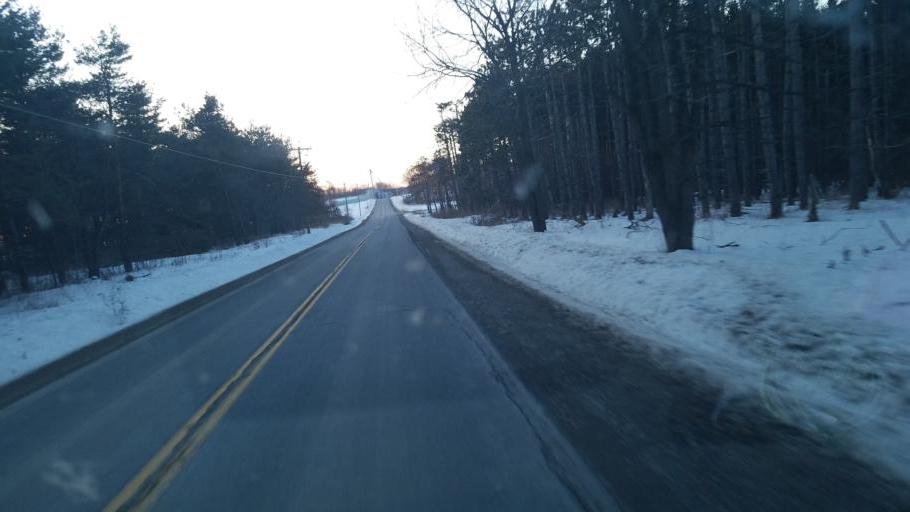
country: US
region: New York
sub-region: Allegany County
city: Andover
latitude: 42.0074
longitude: -77.6989
